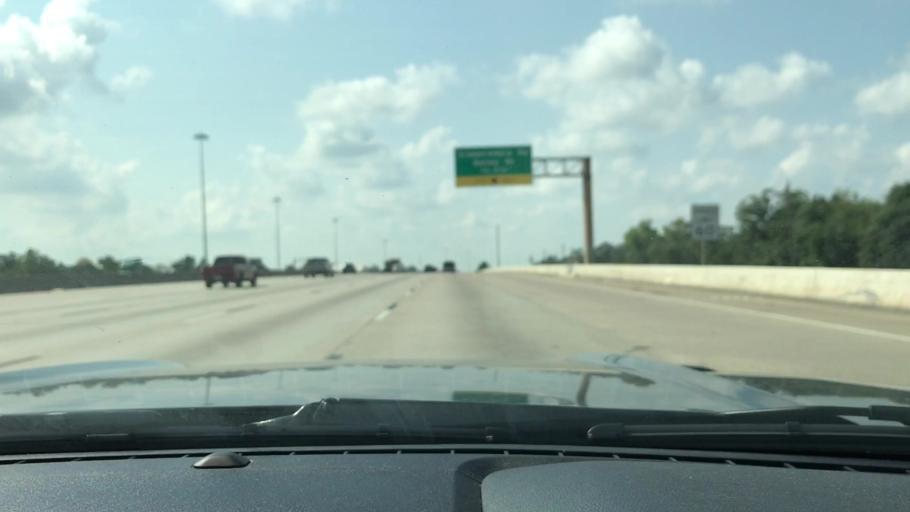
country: US
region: Texas
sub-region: Harris County
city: Houston
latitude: 29.8426
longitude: -95.3339
